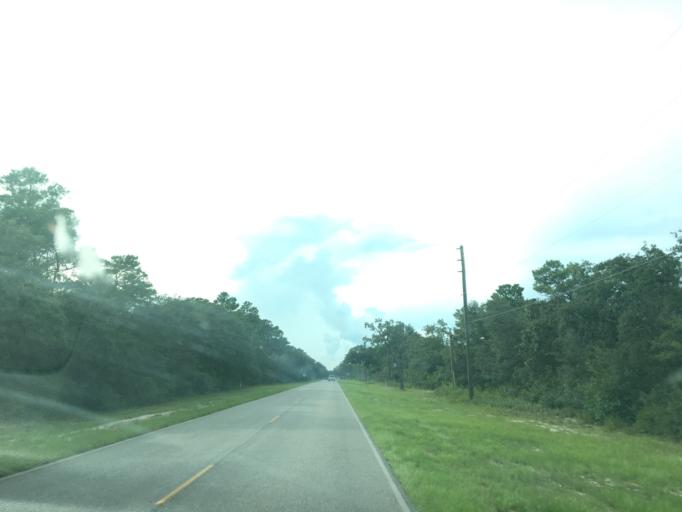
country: US
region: Florida
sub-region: Wakulla County
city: Crawfordville
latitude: 29.9051
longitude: -84.3537
